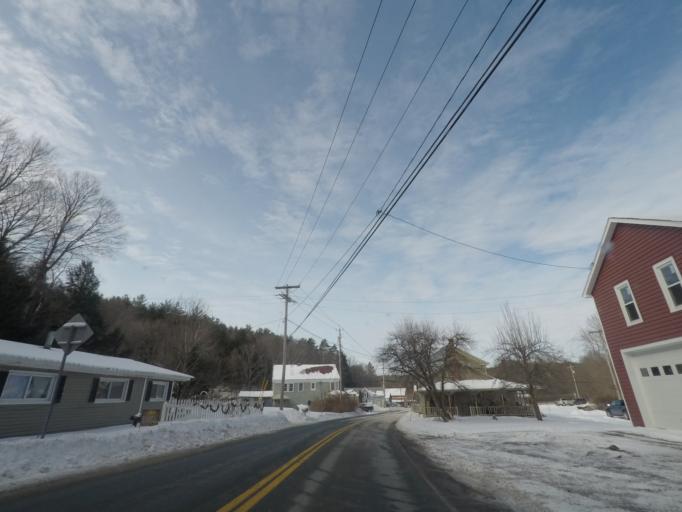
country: US
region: New York
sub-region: Rensselaer County
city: Averill Park
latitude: 42.5559
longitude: -73.5102
